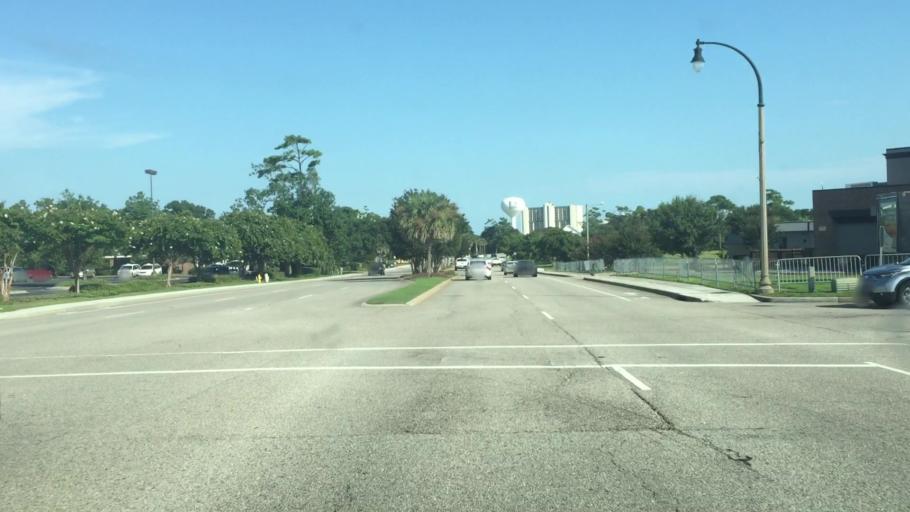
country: US
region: South Carolina
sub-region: Horry County
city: North Myrtle Beach
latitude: 33.8266
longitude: -78.6781
